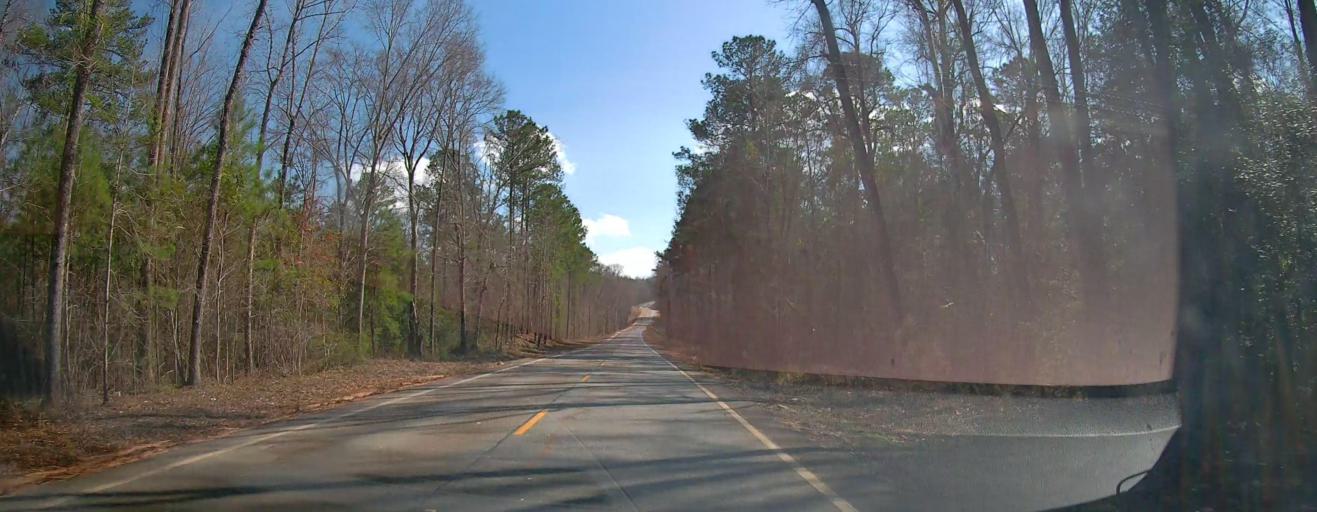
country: US
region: Georgia
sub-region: Wilkinson County
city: Gordon
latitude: 32.8187
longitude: -83.3247
